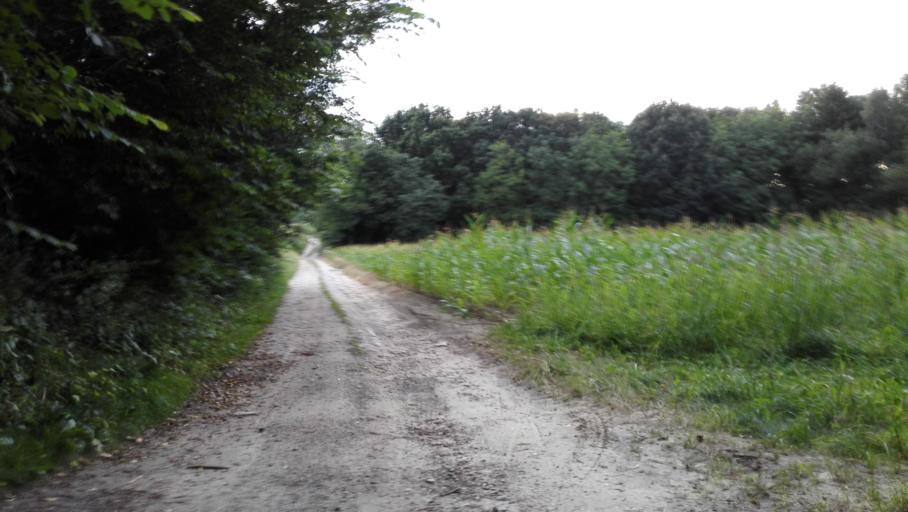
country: BE
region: Flanders
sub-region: Provincie Vlaams-Brabant
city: Bierbeek
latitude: 50.8280
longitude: 4.7410
